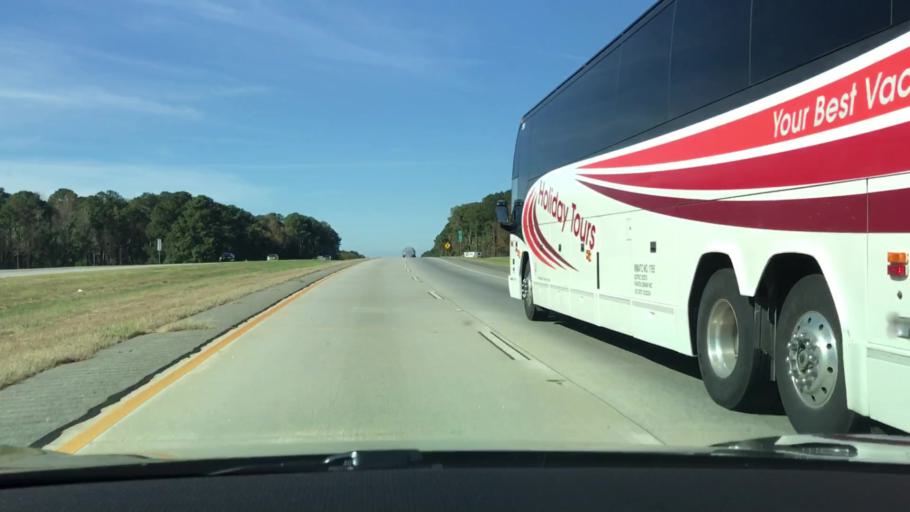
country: US
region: Georgia
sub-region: Greene County
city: Union Point
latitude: 33.5442
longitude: -83.0803
